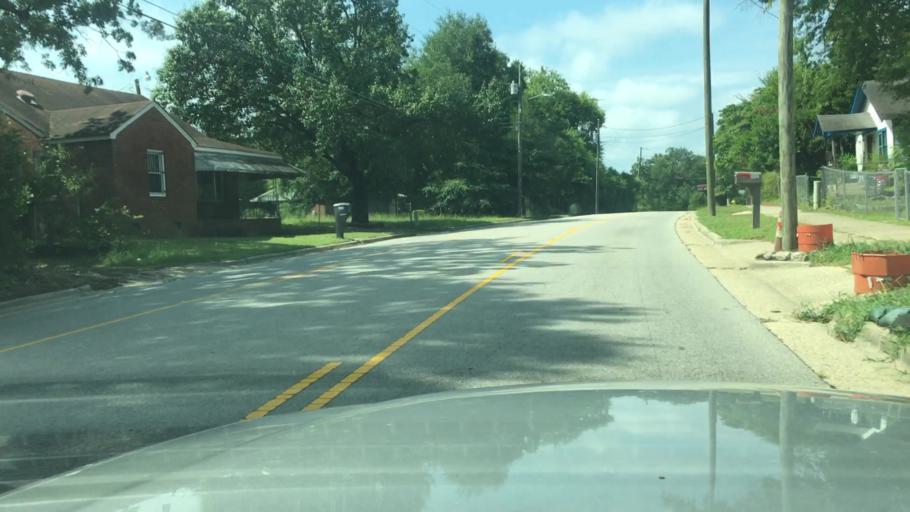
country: US
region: North Carolina
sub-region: Cumberland County
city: Fayetteville
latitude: 35.0270
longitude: -78.8983
